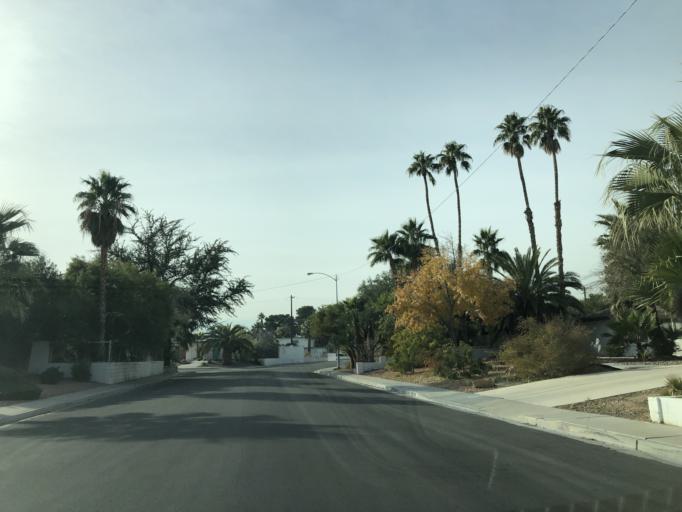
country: US
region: Nevada
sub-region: Clark County
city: Winchester
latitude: 36.1199
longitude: -115.1212
